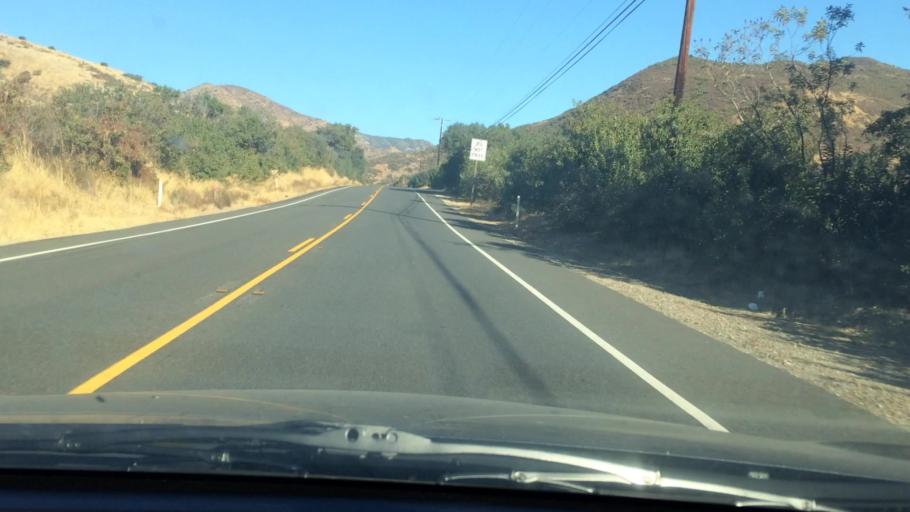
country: US
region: California
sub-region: Orange County
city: Coto De Caza
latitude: 33.5816
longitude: -117.5276
